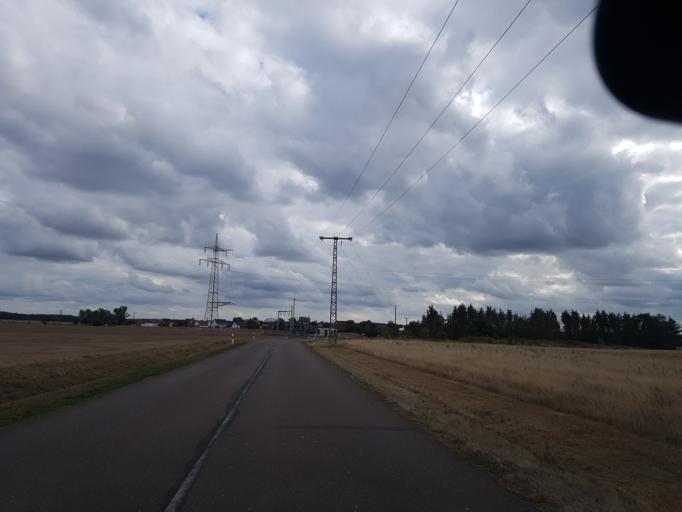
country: DE
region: Saxony-Anhalt
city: Klieken
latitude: 51.9319
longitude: 12.3233
